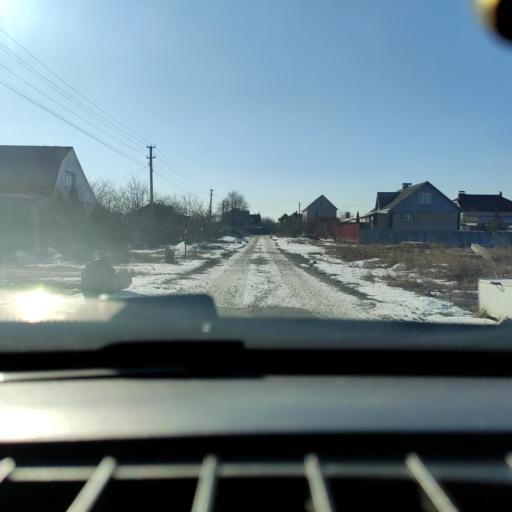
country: RU
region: Voronezj
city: Novaya Usman'
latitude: 51.6649
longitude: 39.3351
